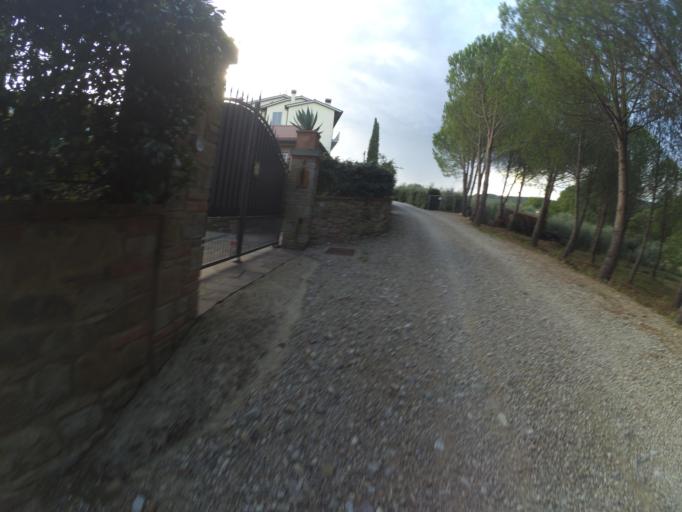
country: IT
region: Tuscany
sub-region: Province of Arezzo
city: Castiglion Fibocchi
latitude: 43.5310
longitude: 11.7674
